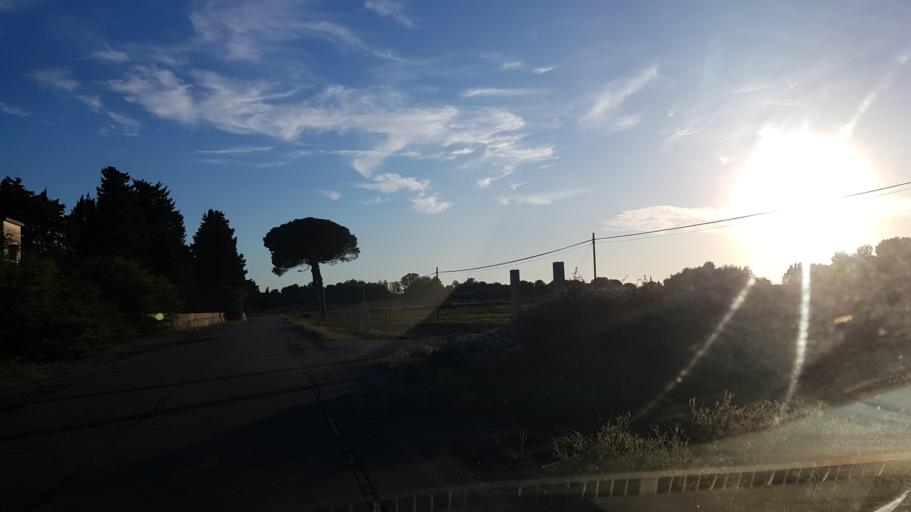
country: IT
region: Apulia
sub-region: Provincia di Lecce
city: Lecce
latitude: 40.3809
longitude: 18.1864
